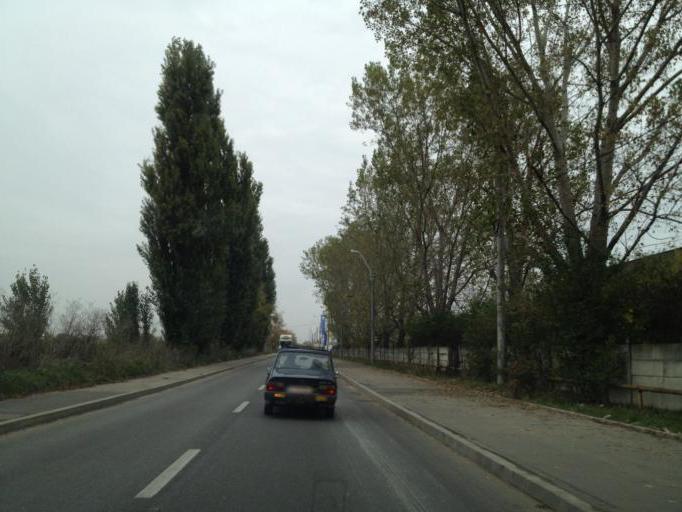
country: RO
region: Dolj
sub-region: Municipiul Craiova
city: Popoveni
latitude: 44.2911
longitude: 23.7918
